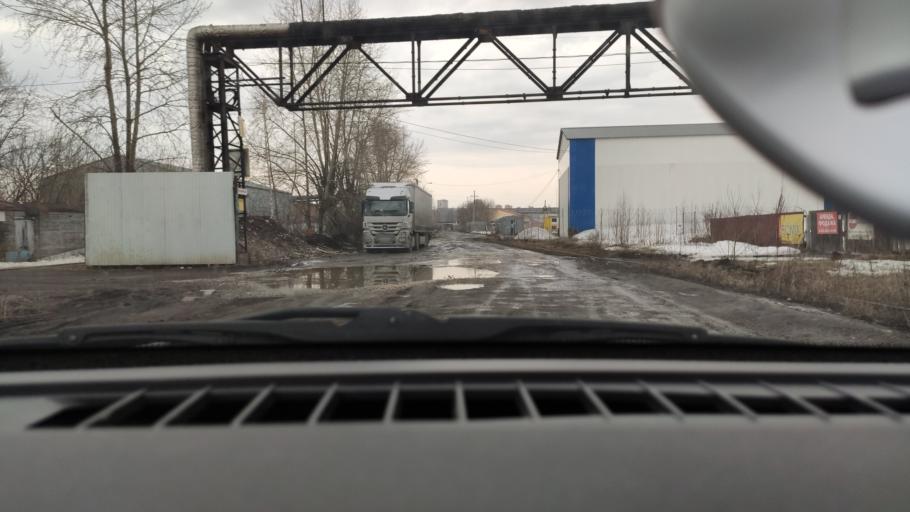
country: RU
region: Perm
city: Perm
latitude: 58.0464
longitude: 56.3151
